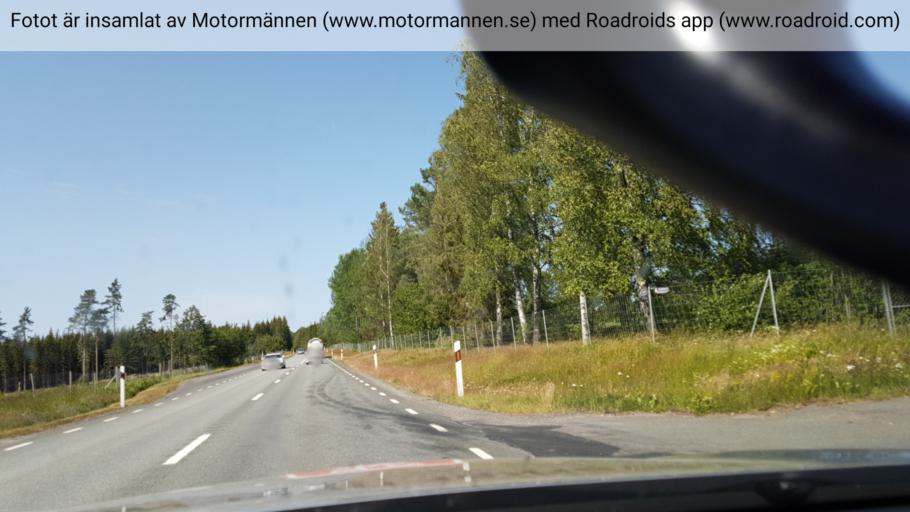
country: SE
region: Joenkoeping
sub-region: Eksjo Kommun
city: Eksjoe
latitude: 57.6957
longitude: 14.9533
